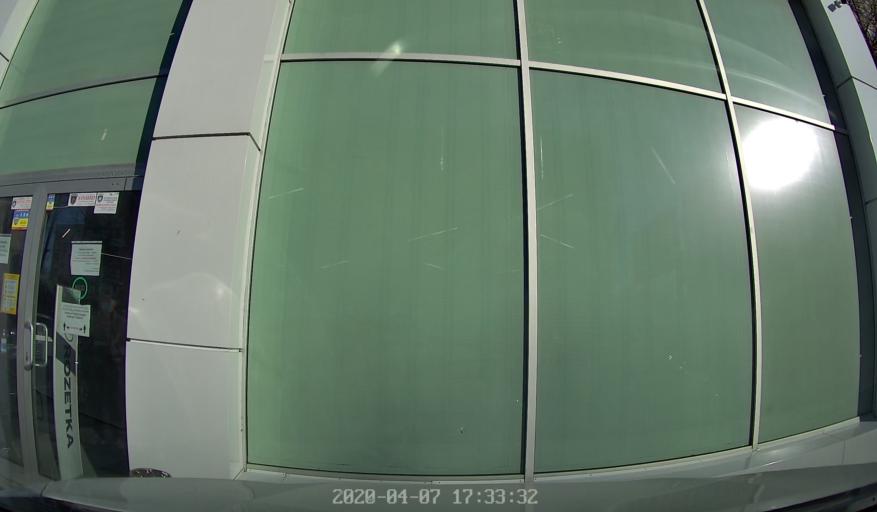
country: GR
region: South Aegean
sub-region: Nomos Kykladon
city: Serifos
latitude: 37.1467
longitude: 24.5659
